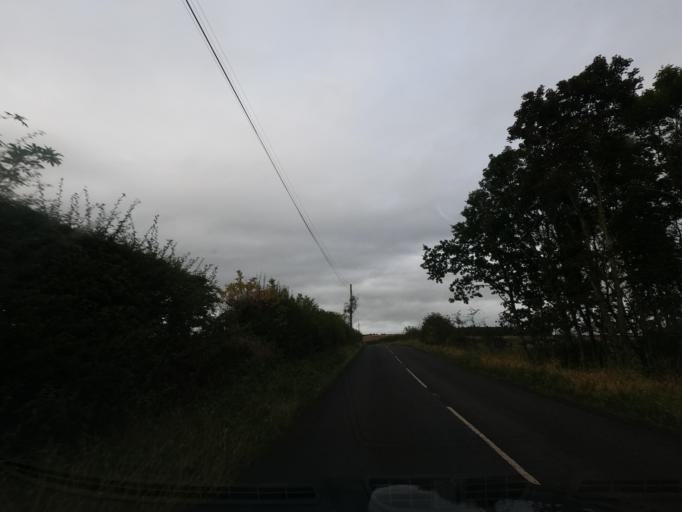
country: GB
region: England
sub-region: Northumberland
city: Doddington
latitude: 55.5896
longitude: -2.0027
